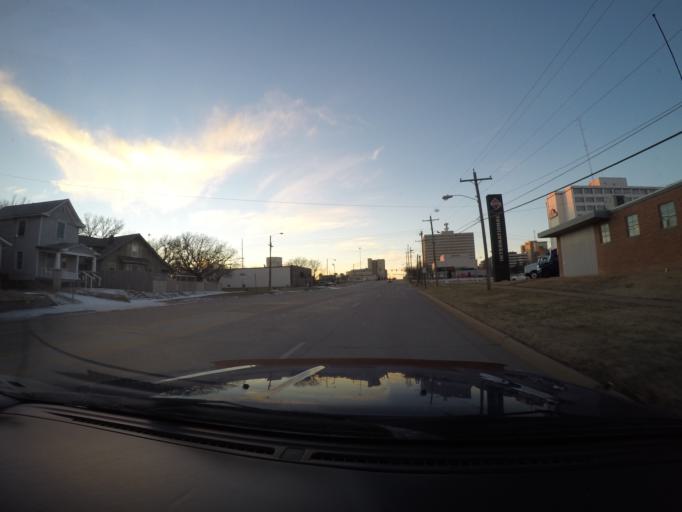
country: US
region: Kansas
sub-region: Shawnee County
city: Topeka
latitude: 39.0444
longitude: -95.6696
